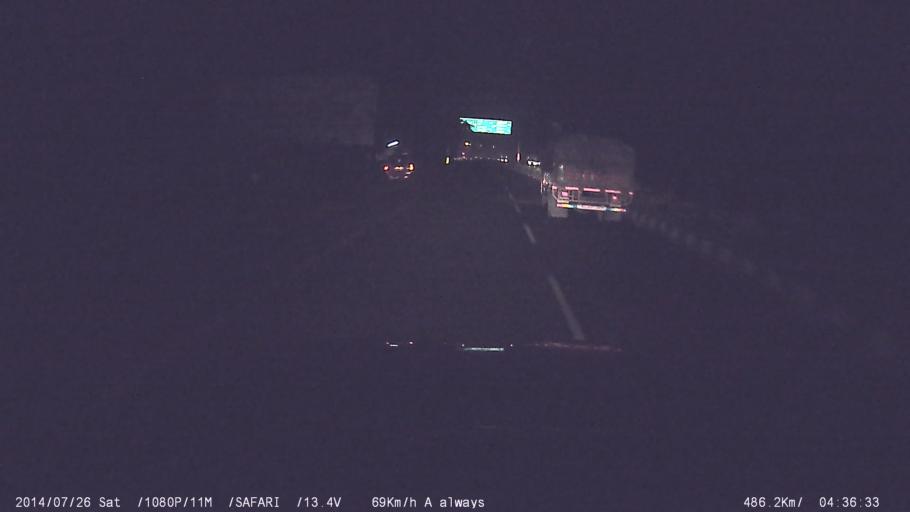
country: IN
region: Kerala
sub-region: Thrissur District
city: Kizhake Chalakudi
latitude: 10.2601
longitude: 76.3607
